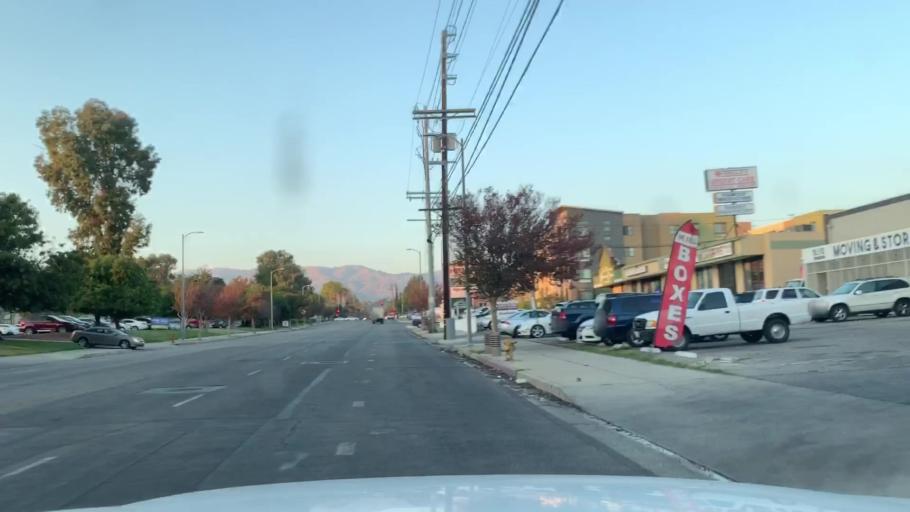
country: US
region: California
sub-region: Los Angeles County
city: Northridge
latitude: 34.2400
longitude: -118.5623
